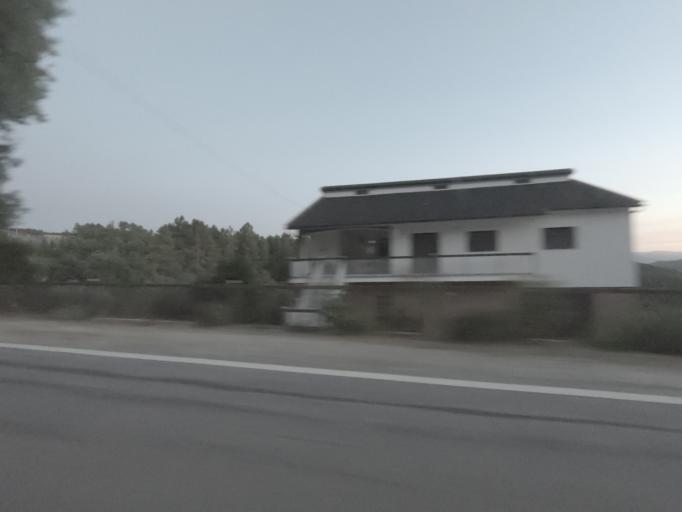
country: PT
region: Vila Real
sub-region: Sabrosa
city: Vilela
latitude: 41.2394
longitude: -7.6857
